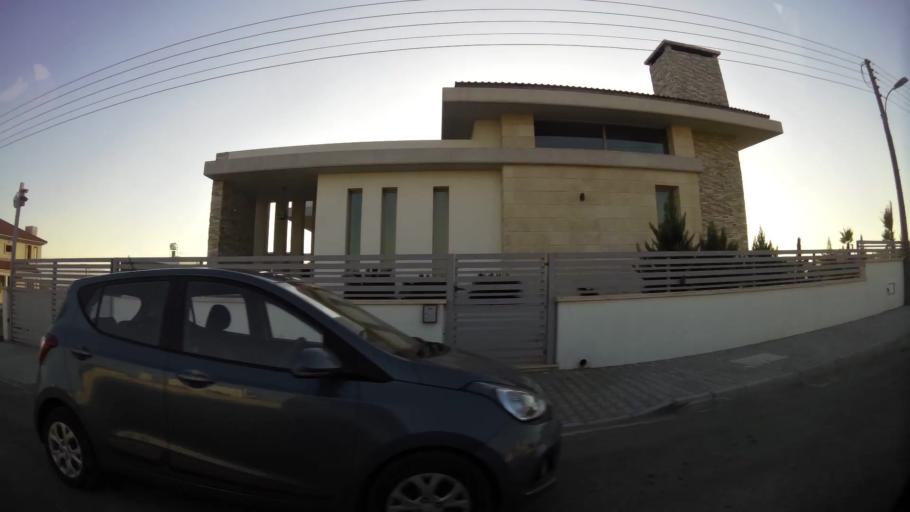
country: CY
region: Lefkosia
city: Nicosia
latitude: 35.1945
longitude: 33.3138
